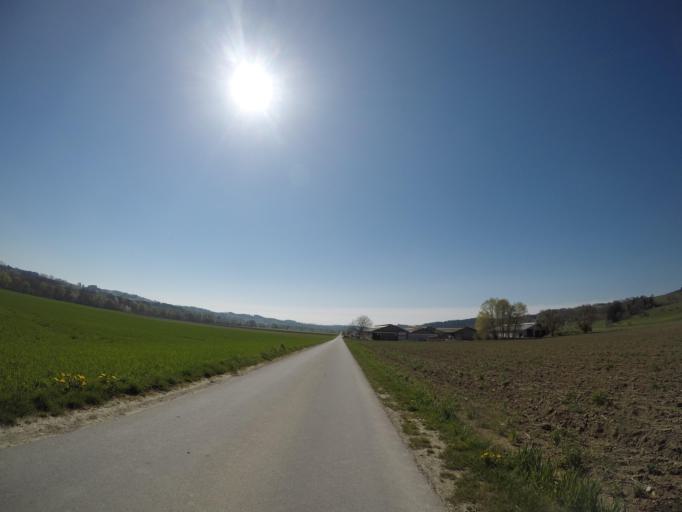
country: DE
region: Baden-Wuerttemberg
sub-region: Tuebingen Region
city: Wilhelmsdorf
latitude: 47.8475
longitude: 9.4382
